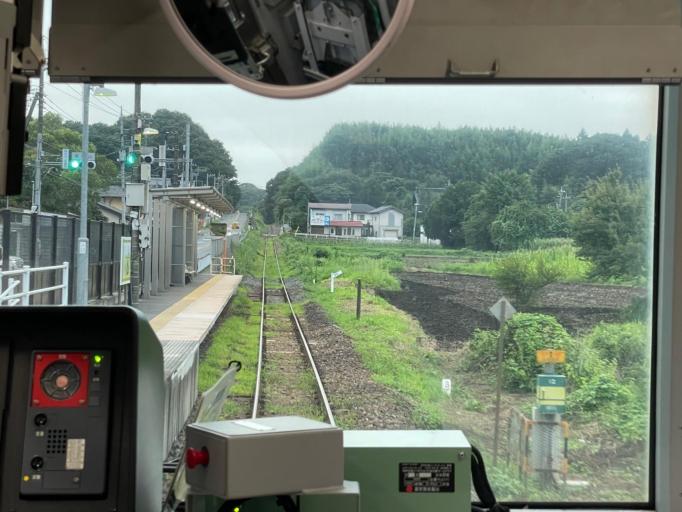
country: JP
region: Tochigi
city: Ujiie
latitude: 36.6664
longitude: 140.0524
